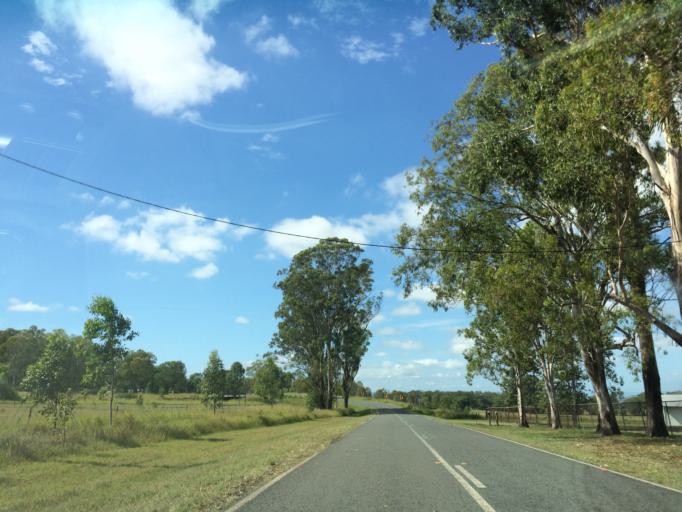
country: AU
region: Queensland
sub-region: Logan
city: Cedar Vale
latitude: -27.8869
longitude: 152.9726
